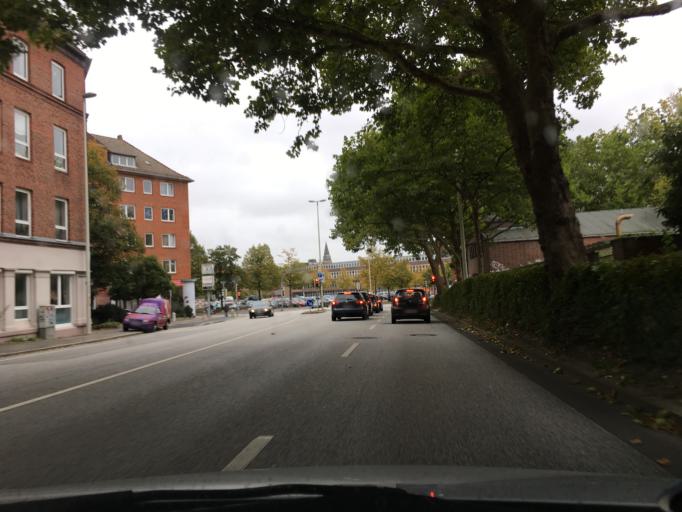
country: DE
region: Schleswig-Holstein
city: Kiel
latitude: 54.3237
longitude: 10.1178
